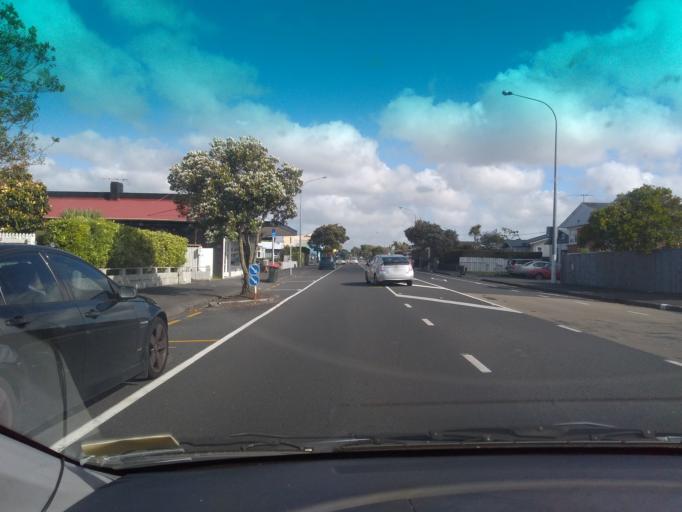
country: NZ
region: Auckland
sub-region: Auckland
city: Rosebank
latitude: -36.8648
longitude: 174.7060
